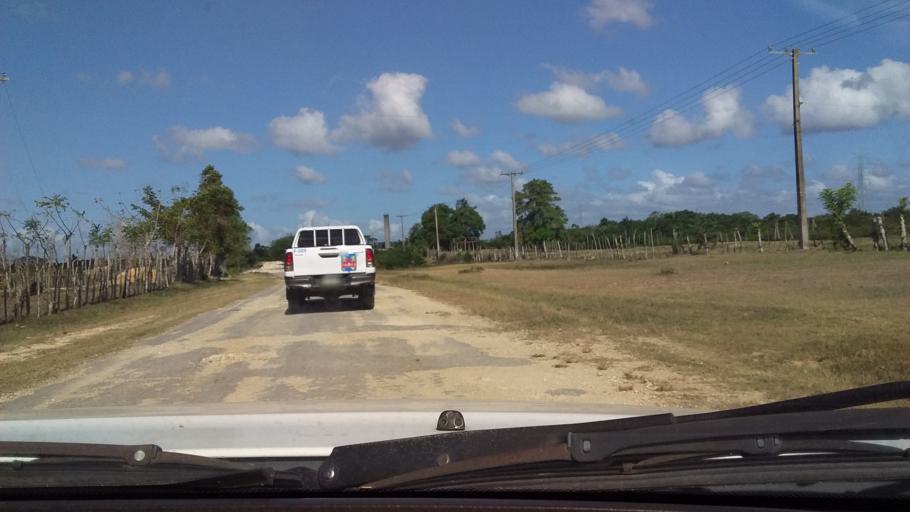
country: DO
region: Santo Domingo
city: Guerra
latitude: 18.5670
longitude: -69.7822
